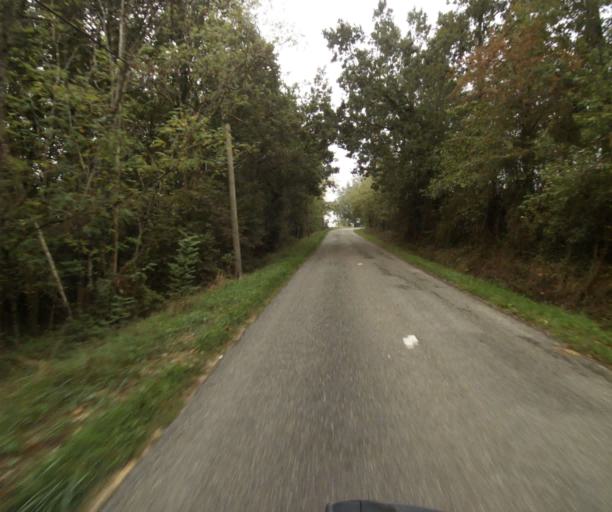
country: FR
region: Midi-Pyrenees
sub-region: Departement du Tarn-et-Garonne
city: Saint-Nauphary
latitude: 43.9363
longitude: 1.4416
